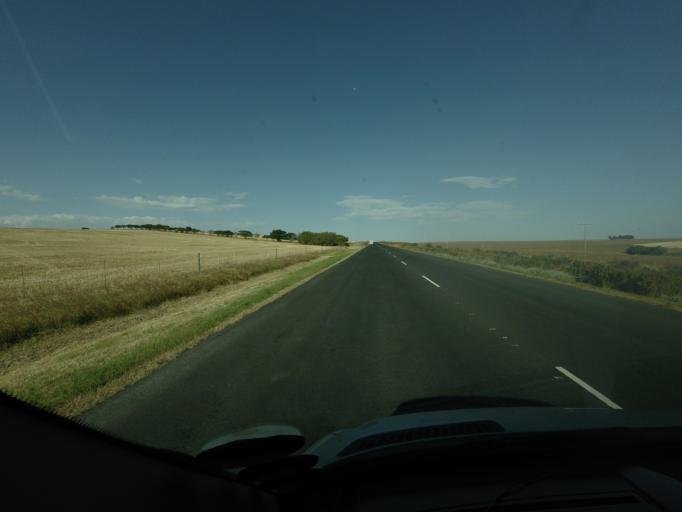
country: ZA
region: Western Cape
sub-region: Cape Winelands District Municipality
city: Ashton
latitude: -34.1413
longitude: 20.0098
